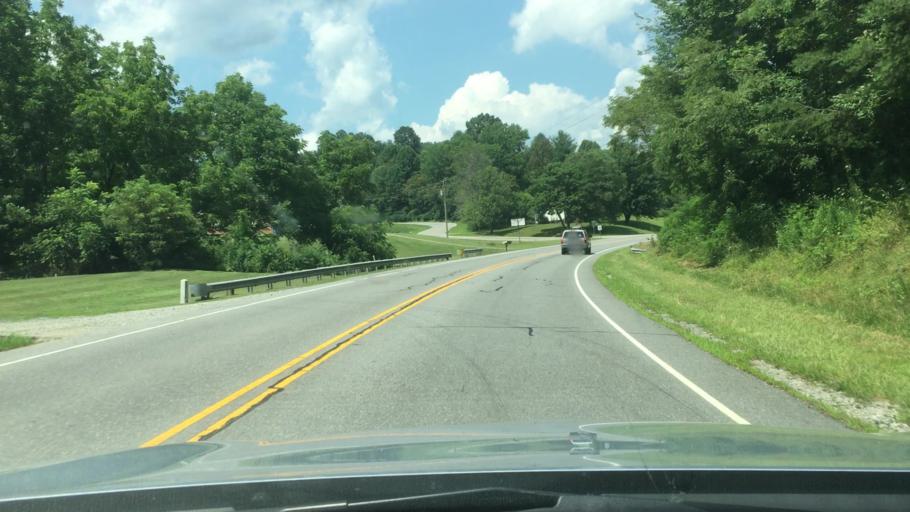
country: US
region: North Carolina
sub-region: Madison County
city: Marshall
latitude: 35.8143
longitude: -82.6548
